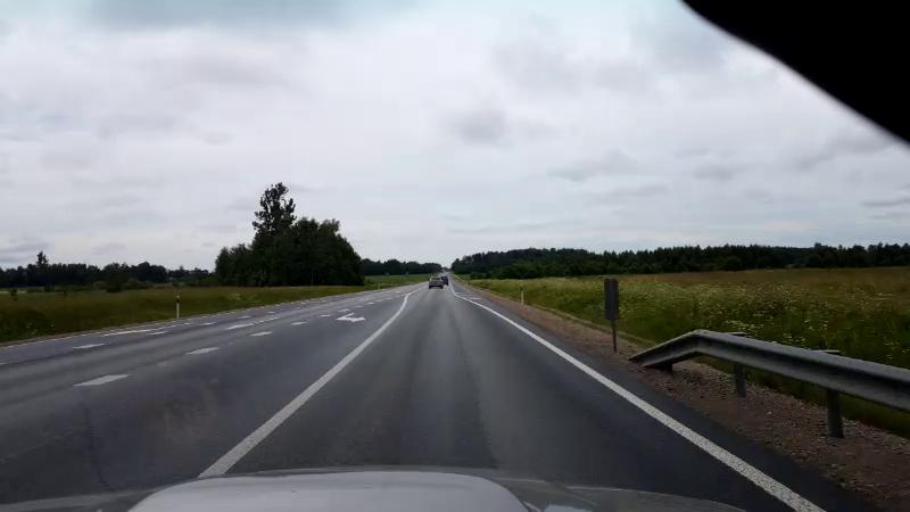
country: LV
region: Lecava
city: Iecava
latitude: 56.6594
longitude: 24.2318
